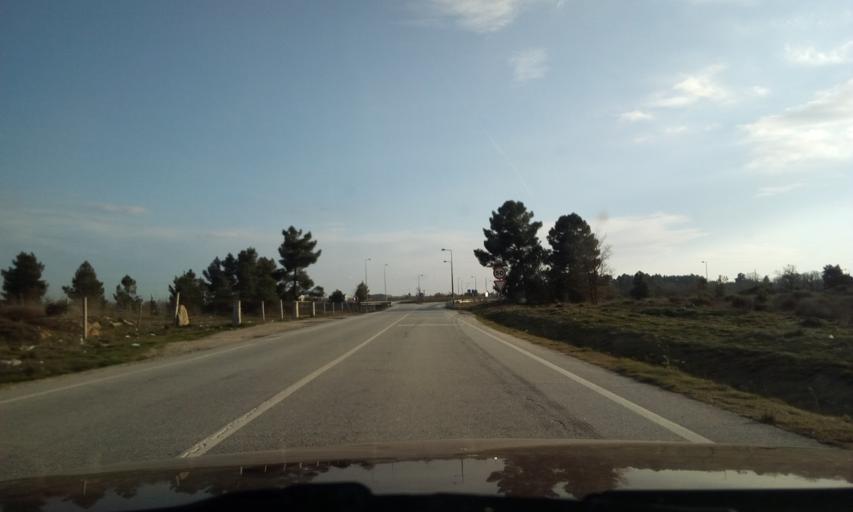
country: ES
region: Castille and Leon
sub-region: Provincia de Salamanca
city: Fuentes de Onoro
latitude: 40.6099
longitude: -6.9823
